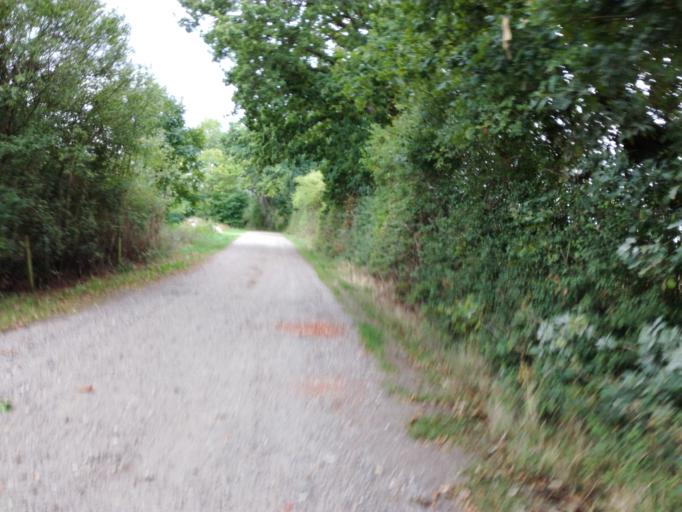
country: DK
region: South Denmark
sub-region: Fredericia Kommune
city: Fredericia
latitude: 55.6057
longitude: 9.7861
